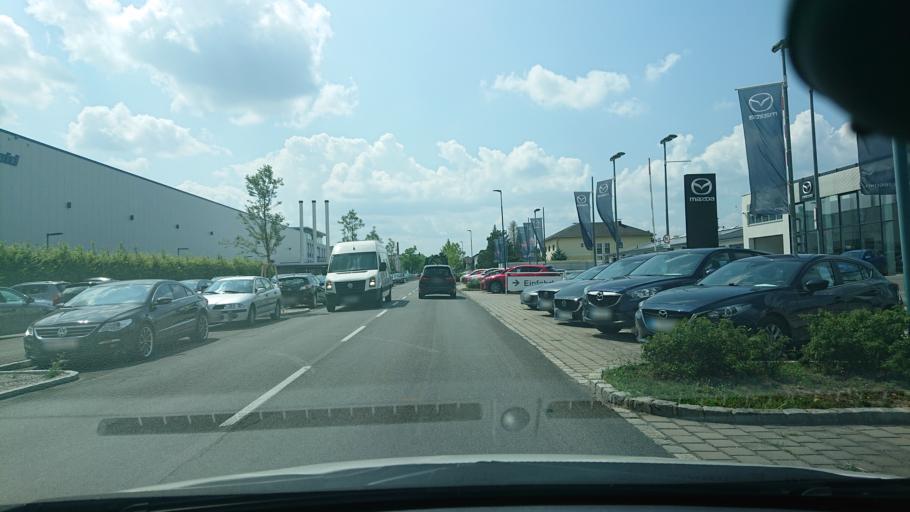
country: AT
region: Lower Austria
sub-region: Politischer Bezirk Baden
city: Kottingbrunn
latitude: 47.9422
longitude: 16.2215
